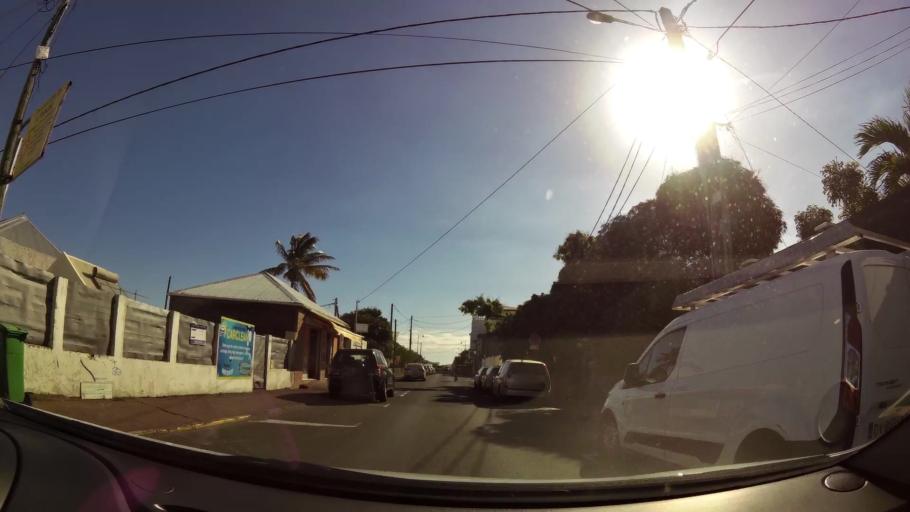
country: RE
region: Reunion
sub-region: Reunion
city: Saint-Pierre
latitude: -21.3403
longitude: 55.4676
